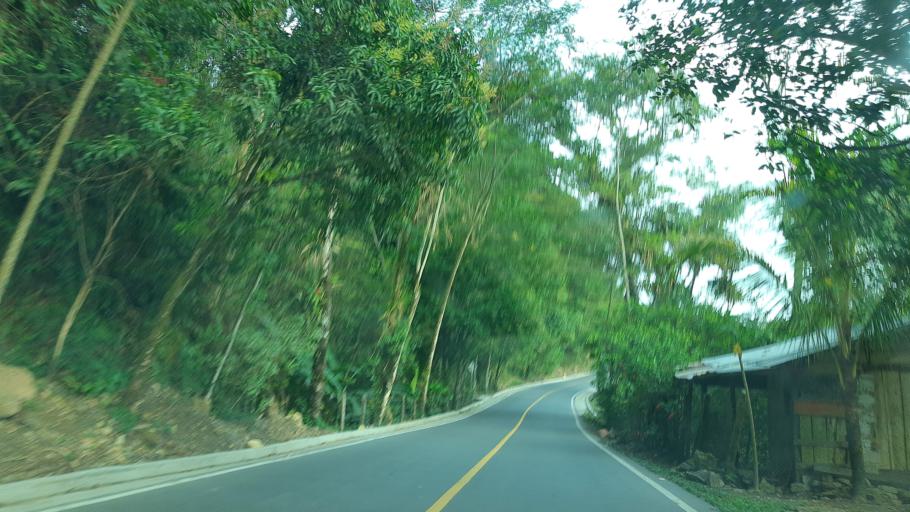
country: CO
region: Boyaca
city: San Luis de Gaceno
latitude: 4.8309
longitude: -73.2068
